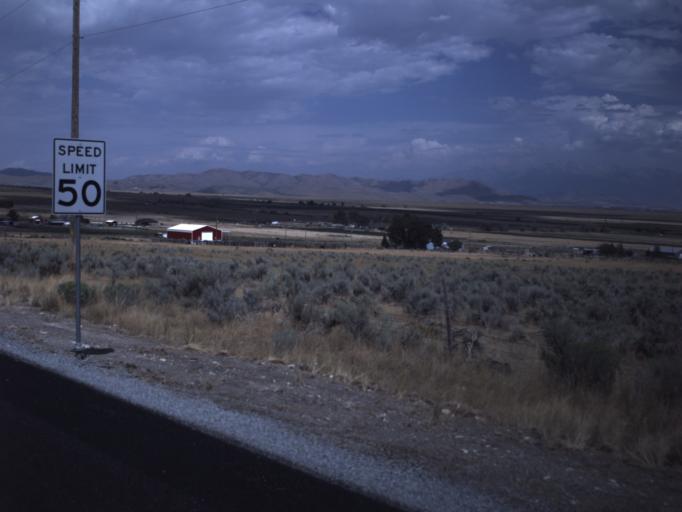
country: US
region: Utah
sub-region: Utah County
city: Eagle Mountain
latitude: 40.3211
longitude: -112.1024
